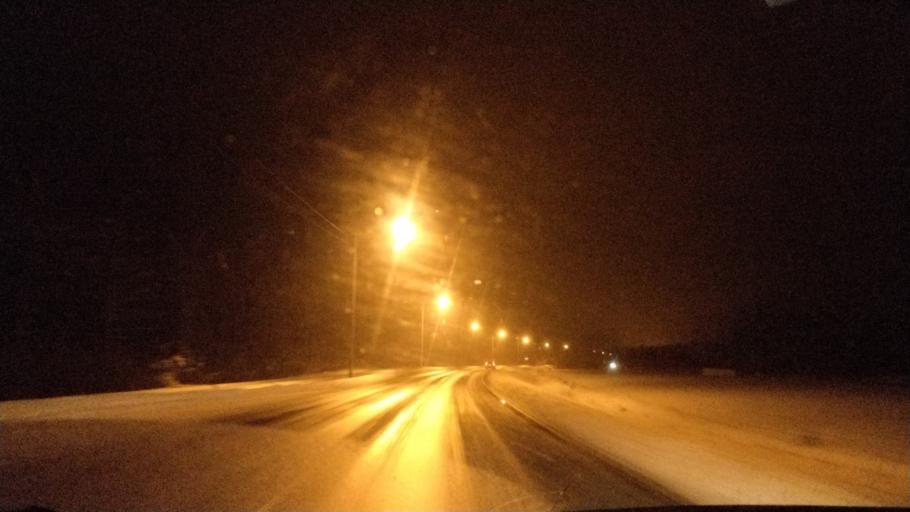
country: FI
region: Lapland
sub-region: Rovaniemi
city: Rovaniemi
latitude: 66.2612
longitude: 25.3416
